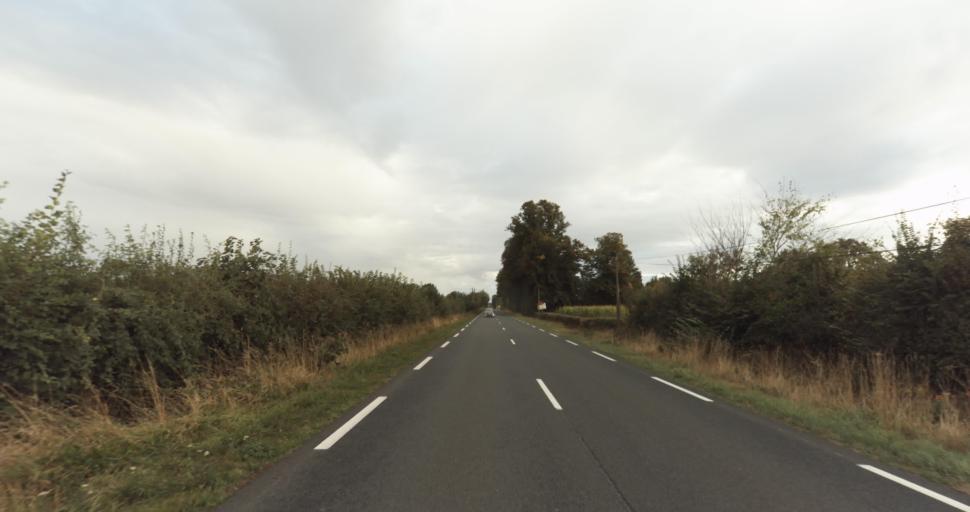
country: FR
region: Lower Normandy
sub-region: Departement de l'Orne
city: Vimoutiers
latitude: 48.8885
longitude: 0.2557
